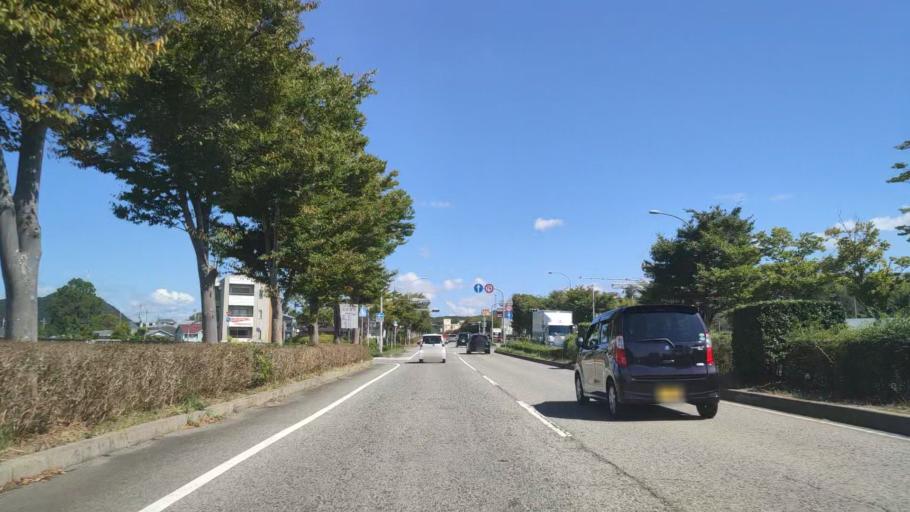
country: JP
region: Hyogo
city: Yashiro
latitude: 34.9361
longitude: 134.9628
